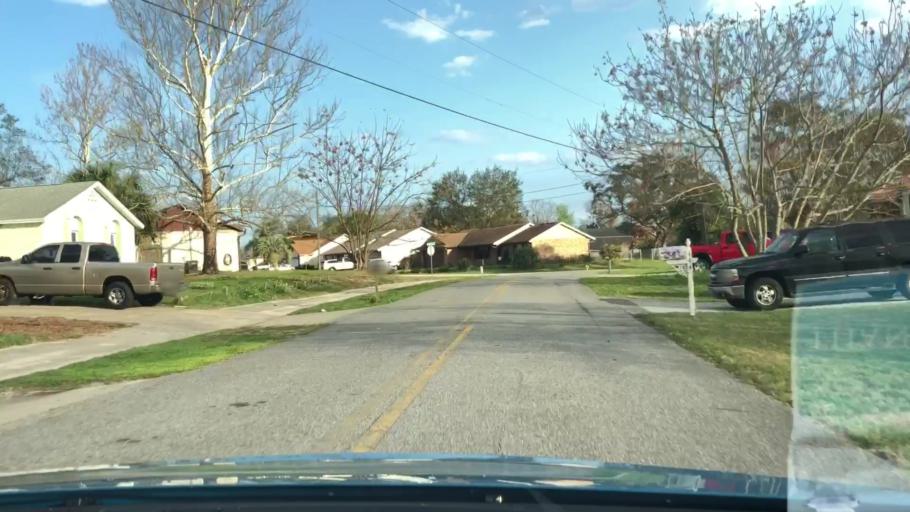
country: US
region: Florida
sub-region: Volusia County
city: Deltona
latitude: 28.8748
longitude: -81.2461
